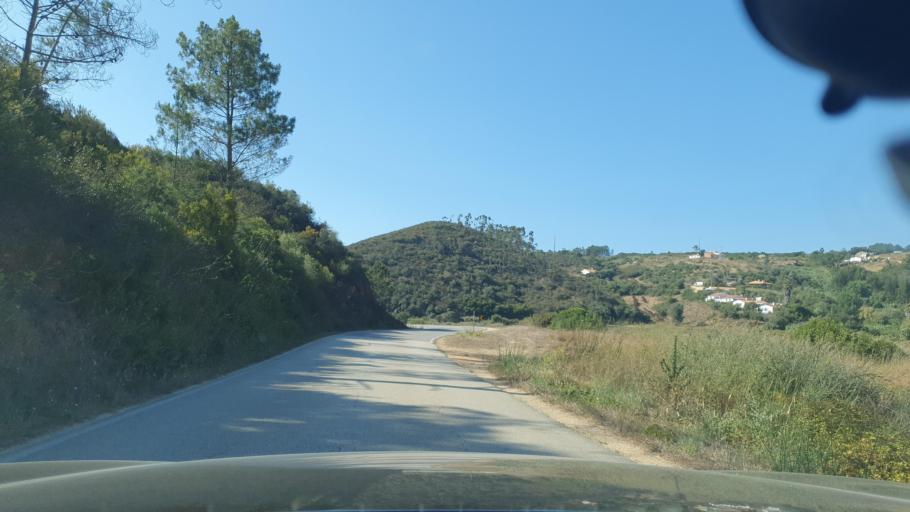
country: PT
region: Beja
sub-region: Odemira
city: Sao Teotonio
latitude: 37.4338
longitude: -8.7851
